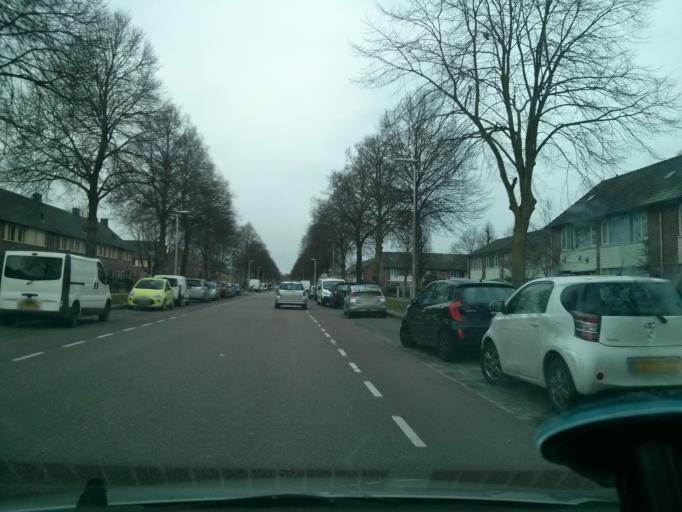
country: NL
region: North Brabant
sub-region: Gemeente Eindhoven
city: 't Hofke
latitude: 51.4778
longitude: 5.5009
